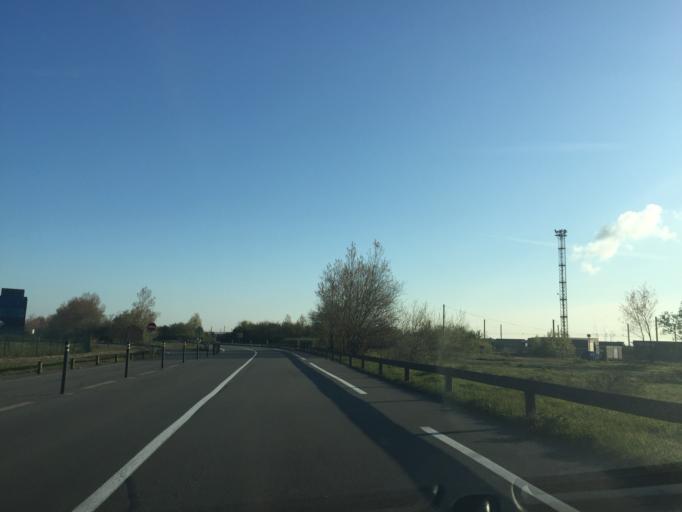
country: FR
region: Nord-Pas-de-Calais
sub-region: Departement du Nord
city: Loon-Plage
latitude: 51.0025
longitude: 2.1974
